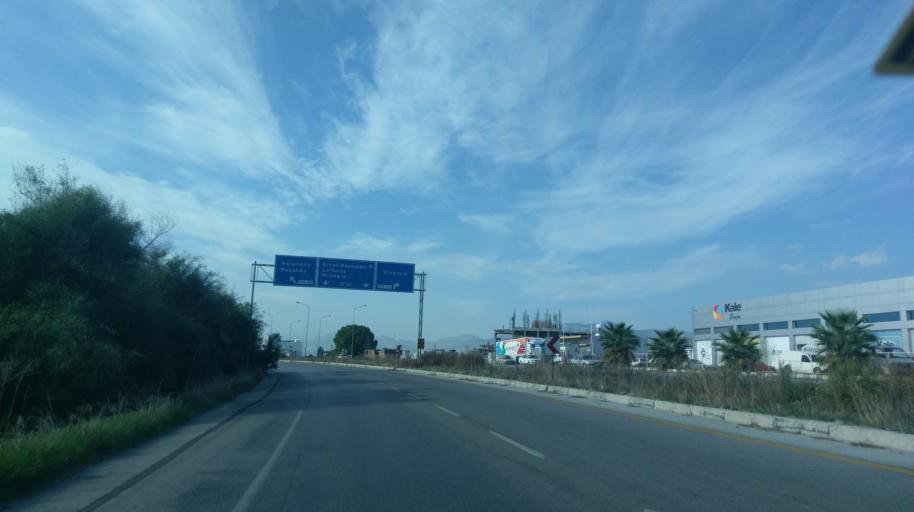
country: CY
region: Ammochostos
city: Lefkonoiko
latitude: 35.2070
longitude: 33.5948
